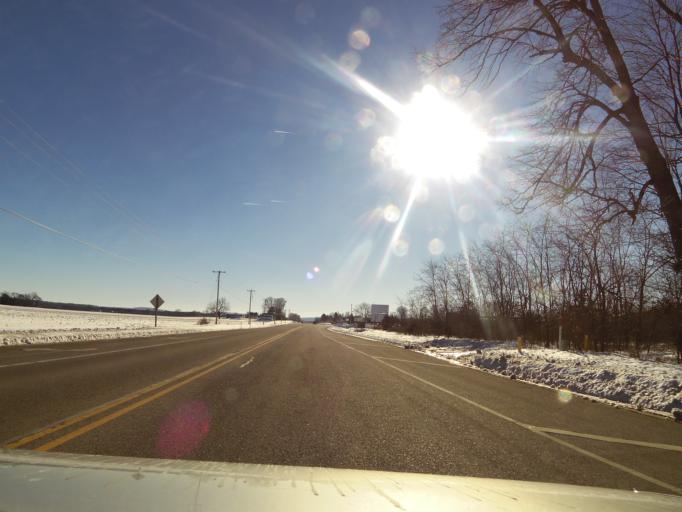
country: US
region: Wisconsin
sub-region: Sauk County
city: West Baraboo
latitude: 43.5102
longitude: -89.7781
